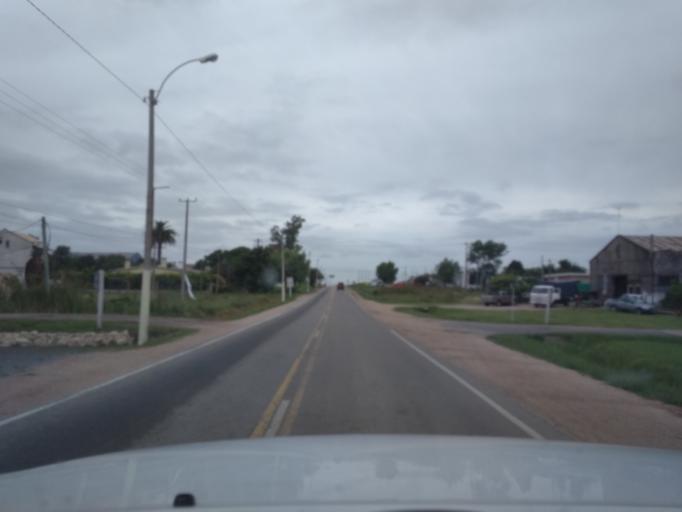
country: UY
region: Canelones
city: Tala
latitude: -34.3484
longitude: -55.7665
